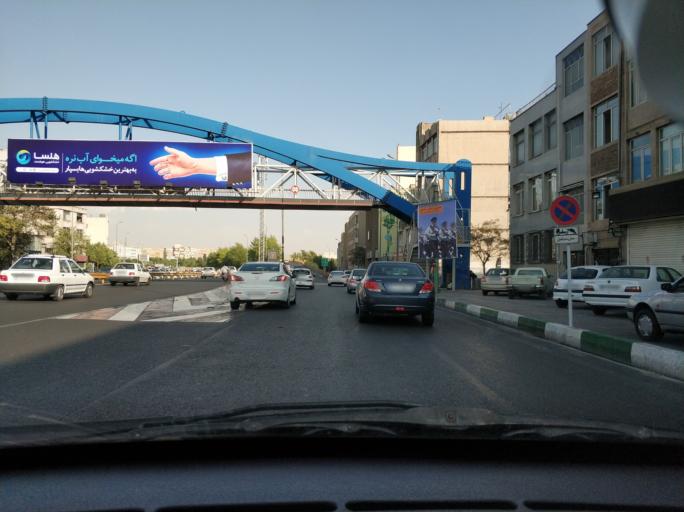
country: IR
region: Tehran
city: Tehran
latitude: 35.7411
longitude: 51.4567
